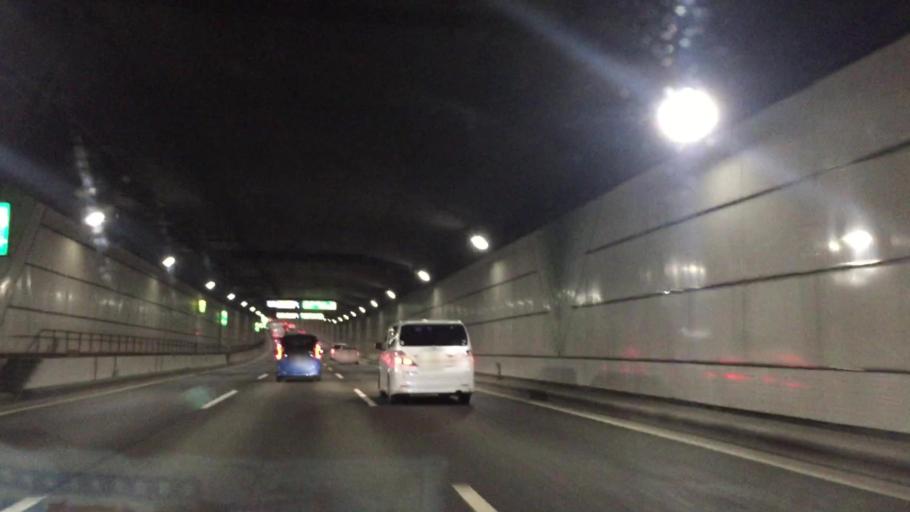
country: JP
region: Kanagawa
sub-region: Kawasaki-shi
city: Kawasaki
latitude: 35.5227
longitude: 139.7922
